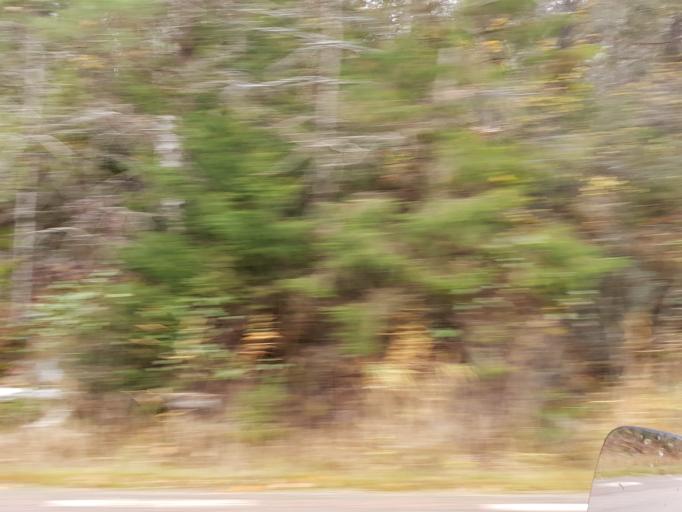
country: SE
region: Vaestra Goetaland
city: Svanesund
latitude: 58.2084
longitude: 11.8225
